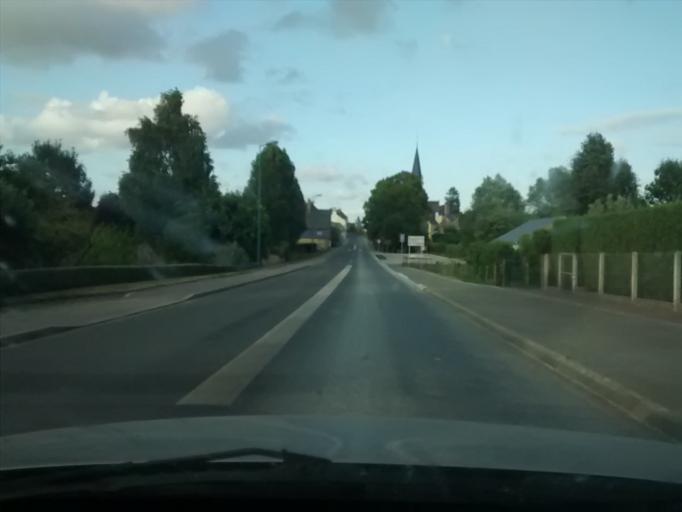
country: FR
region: Pays de la Loire
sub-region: Departement de la Sarthe
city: Sille-le-Guillaume
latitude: 48.1585
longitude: -0.2029
